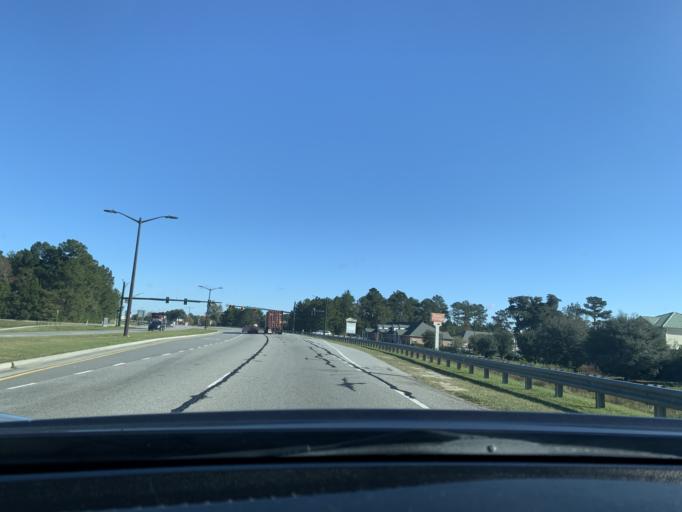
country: US
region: Georgia
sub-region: Chatham County
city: Pooler
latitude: 32.1292
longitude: -81.2582
